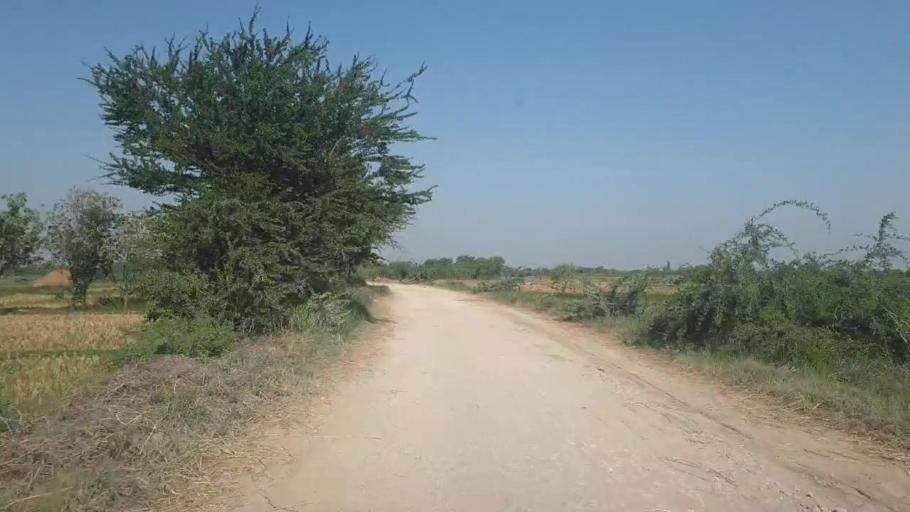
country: PK
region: Sindh
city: Badin
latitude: 24.6734
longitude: 68.8586
